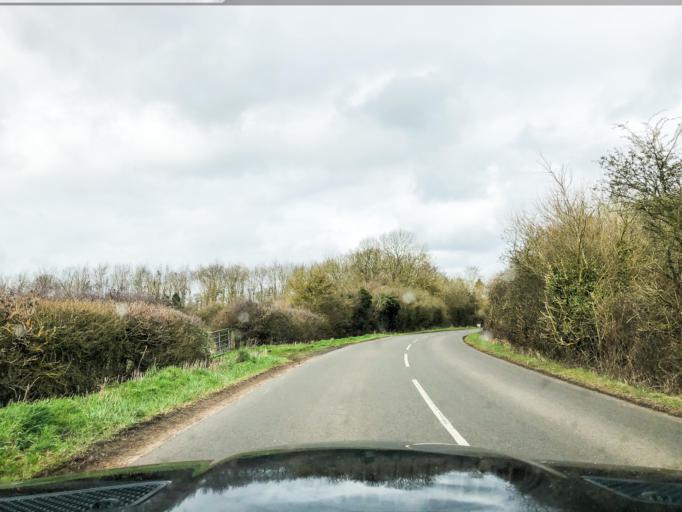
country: GB
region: England
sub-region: Warwickshire
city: Harbury
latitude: 52.1432
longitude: -1.4460
